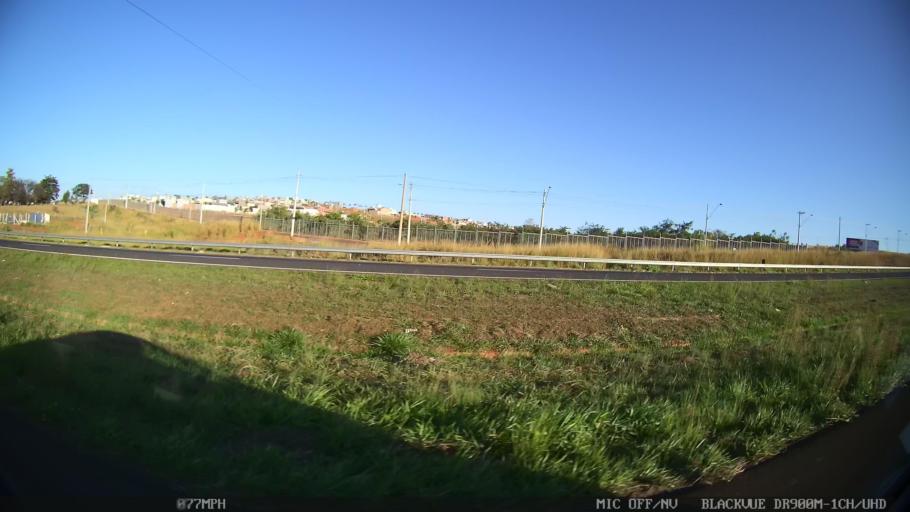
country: BR
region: Sao Paulo
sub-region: Sao Jose Do Rio Preto
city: Sao Jose do Rio Preto
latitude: -20.7973
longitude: -49.3241
